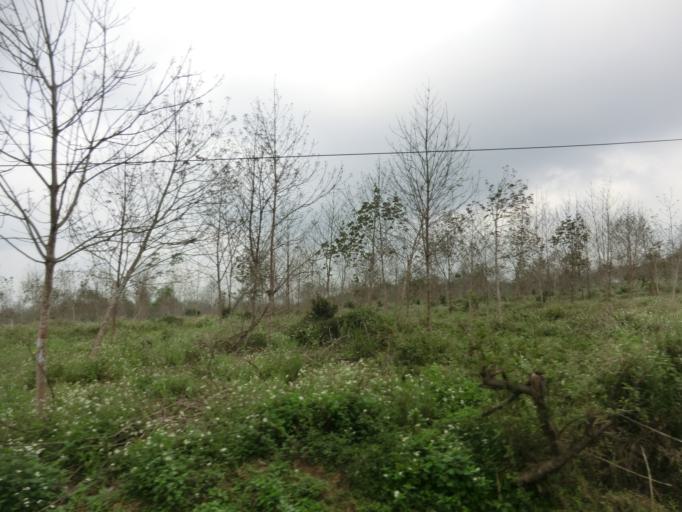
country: VN
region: Quang Binh
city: Ba Don
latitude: 17.6410
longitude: 106.4343
